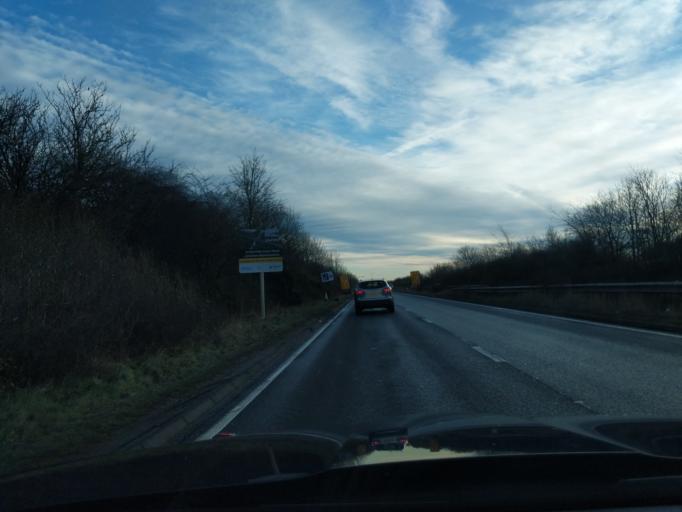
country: GB
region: England
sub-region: Borough of North Tyneside
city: Shiremoor
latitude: 55.0188
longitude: -1.5116
